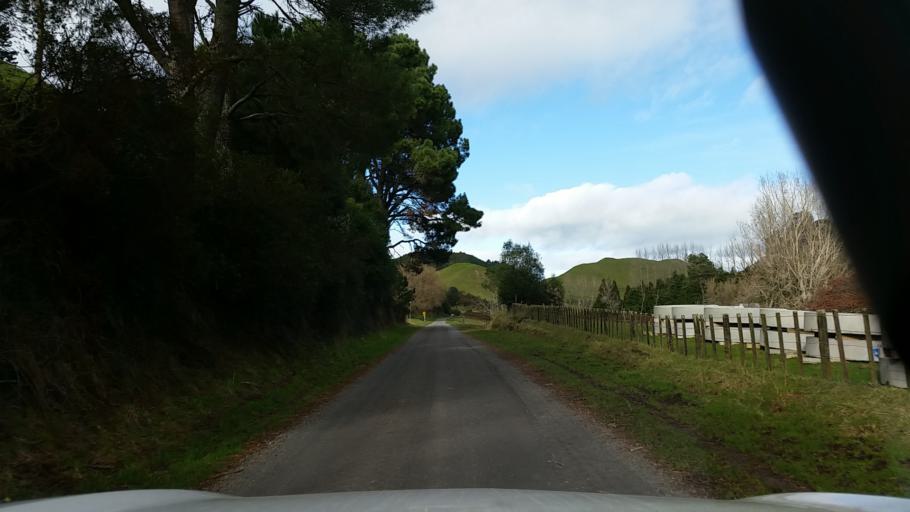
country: NZ
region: Waikato
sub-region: Taupo District
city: Taupo
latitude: -38.4614
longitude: 176.2409
